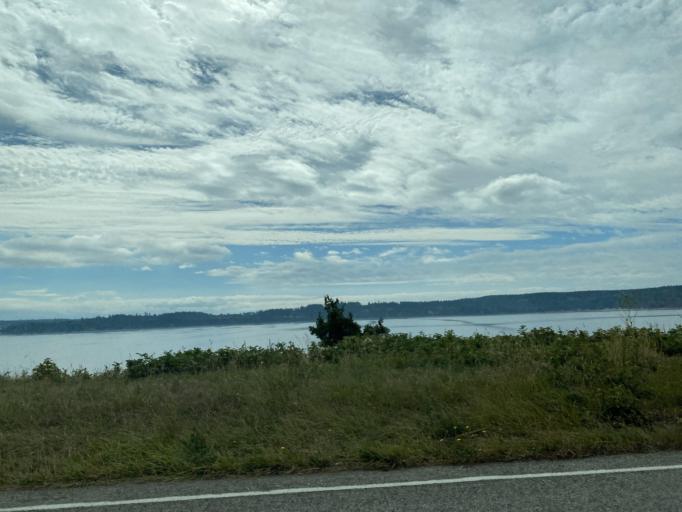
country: US
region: Washington
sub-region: Island County
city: Coupeville
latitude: 48.2365
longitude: -122.7187
